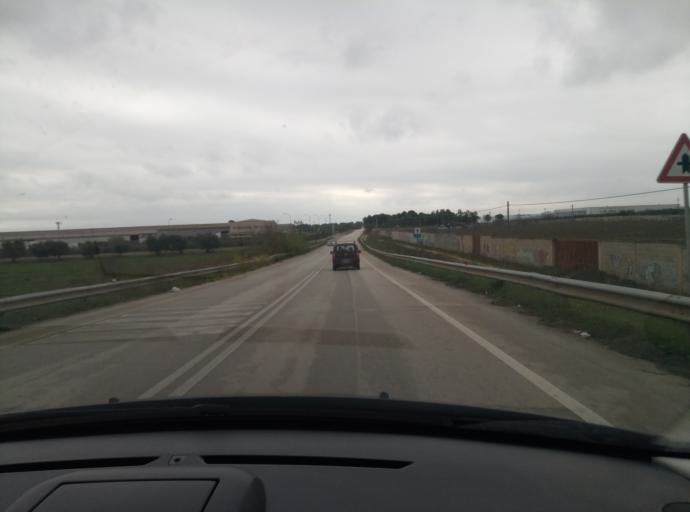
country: IT
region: Apulia
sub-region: Provincia di Bari
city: Acquaviva delle Fonti
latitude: 40.9191
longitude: 16.8557
